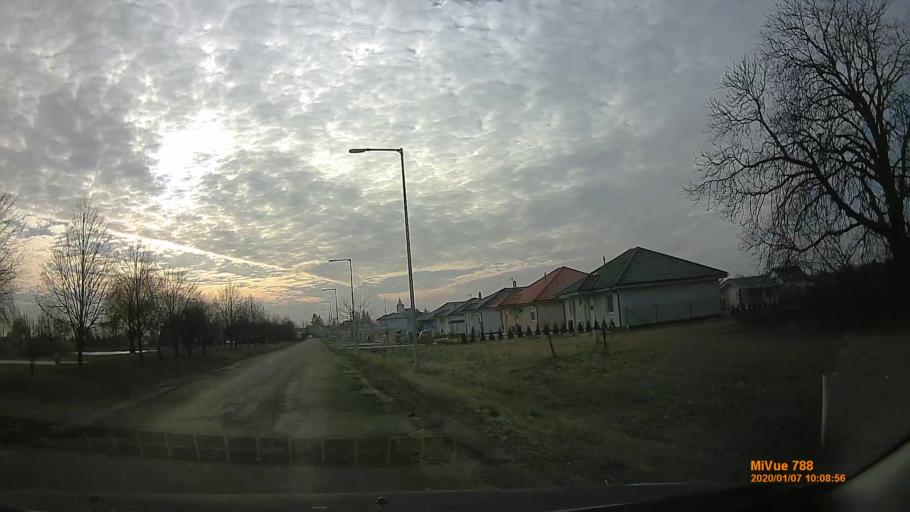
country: AT
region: Burgenland
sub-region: Politischer Bezirk Neusiedl am See
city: Nickelsdorf
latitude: 47.9190
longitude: 17.1543
